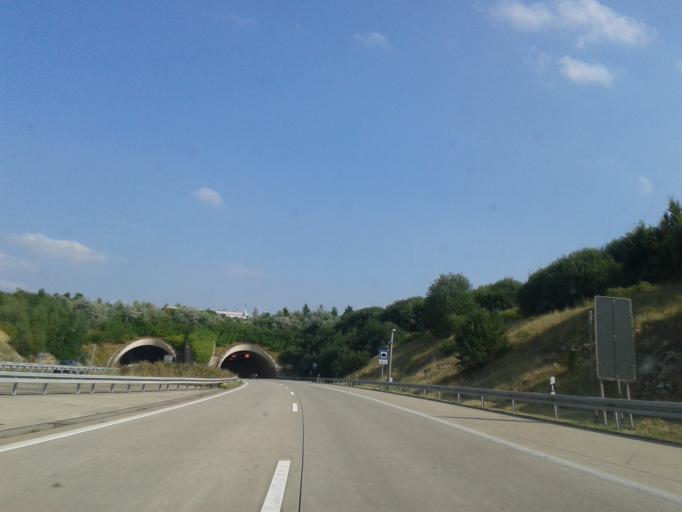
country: DE
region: Saxony
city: Freital
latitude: 51.0293
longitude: 13.6726
